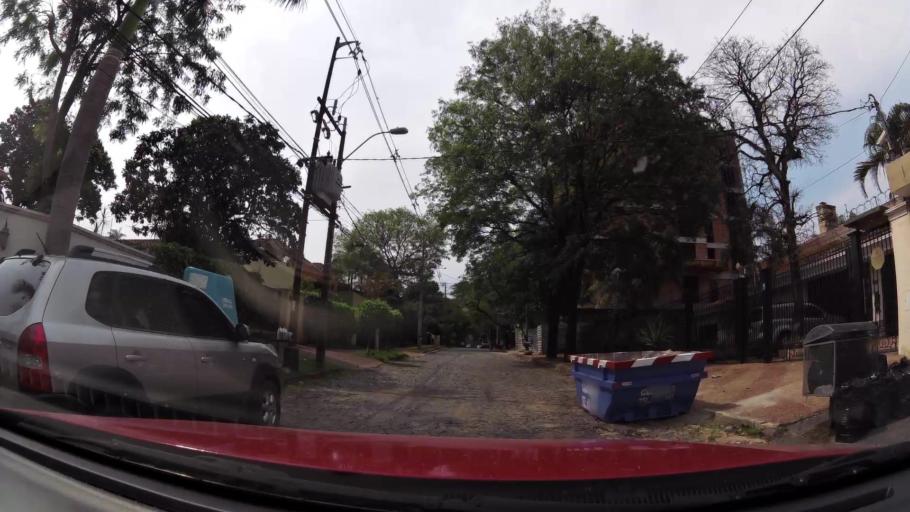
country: PY
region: Asuncion
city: Asuncion
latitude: -25.2839
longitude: -57.5695
